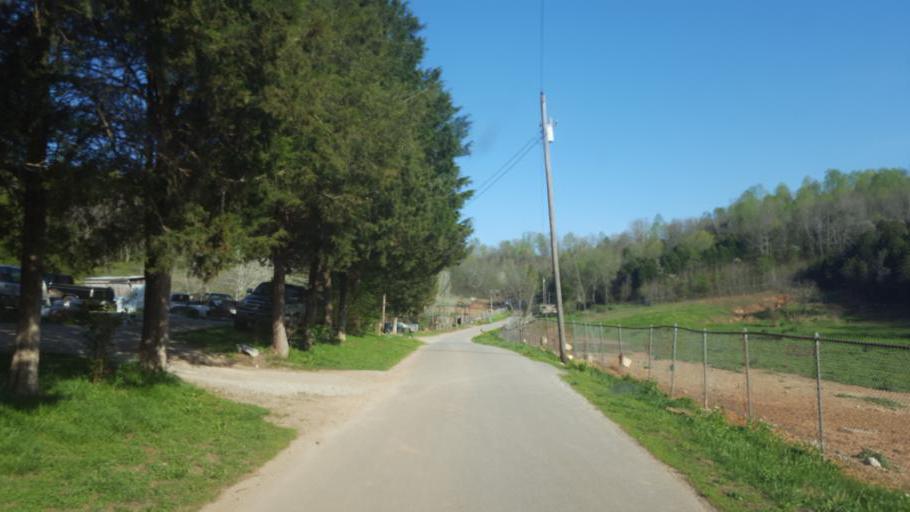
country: US
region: Kentucky
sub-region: Barren County
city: Cave City
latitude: 37.1781
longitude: -86.0057
